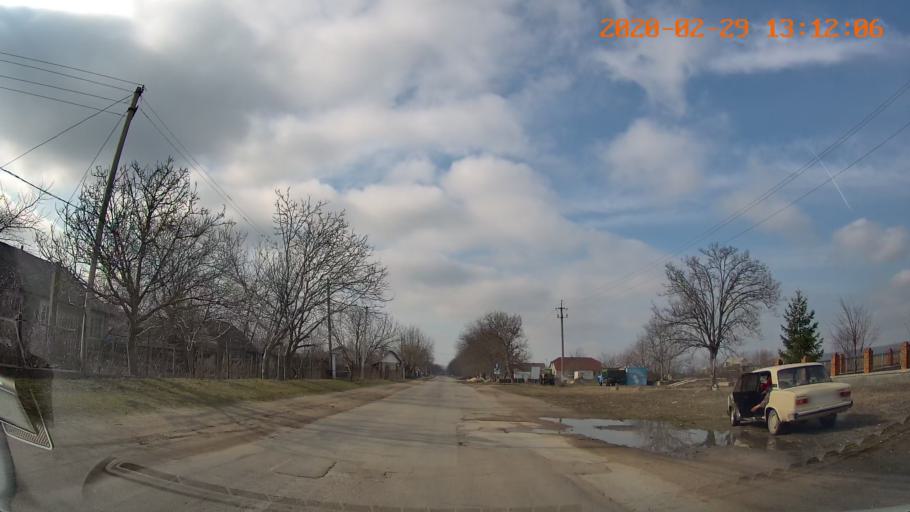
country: MD
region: Telenesti
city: Camenca
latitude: 48.0128
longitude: 28.6976
